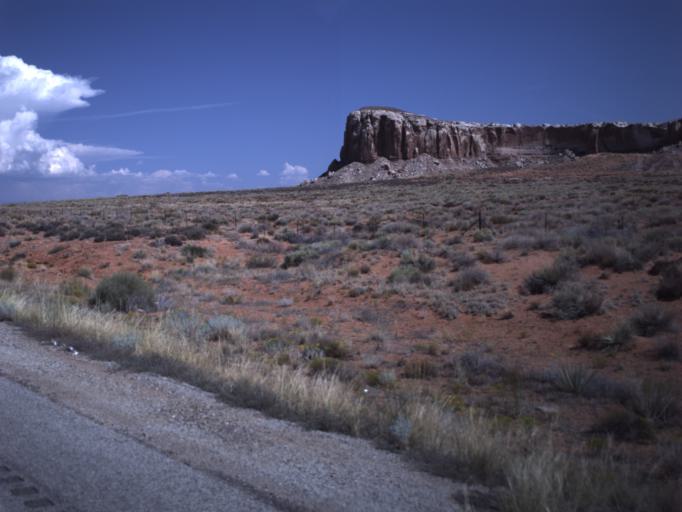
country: US
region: Utah
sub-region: San Juan County
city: Blanding
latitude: 37.2248
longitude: -109.6176
